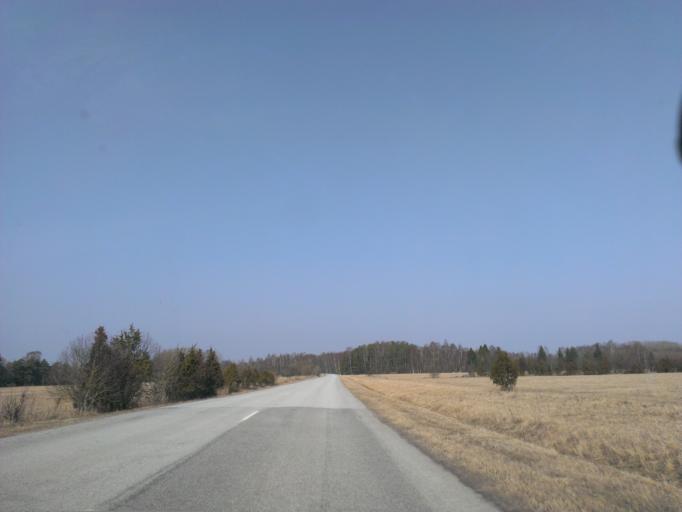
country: EE
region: Saare
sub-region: Orissaare vald
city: Orissaare
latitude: 58.5193
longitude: 23.1062
